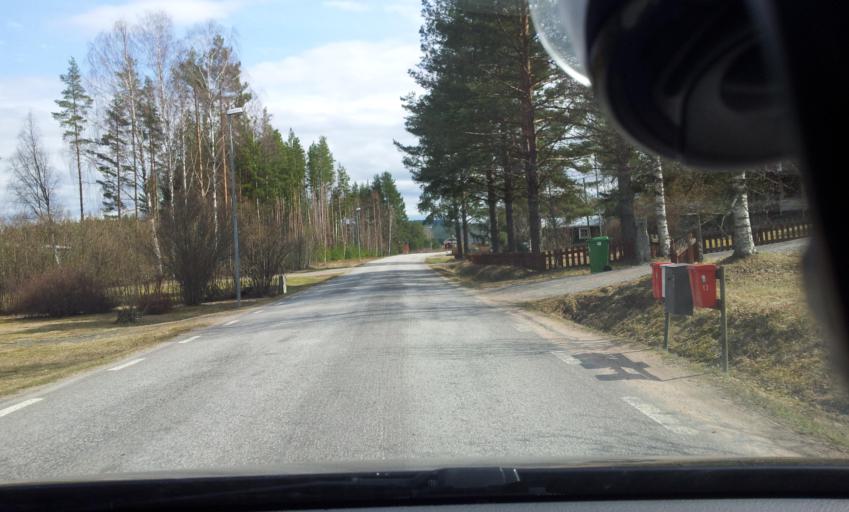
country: SE
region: Gaevleborg
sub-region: Ljusdals Kommun
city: Farila
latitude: 61.8008
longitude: 15.9012
